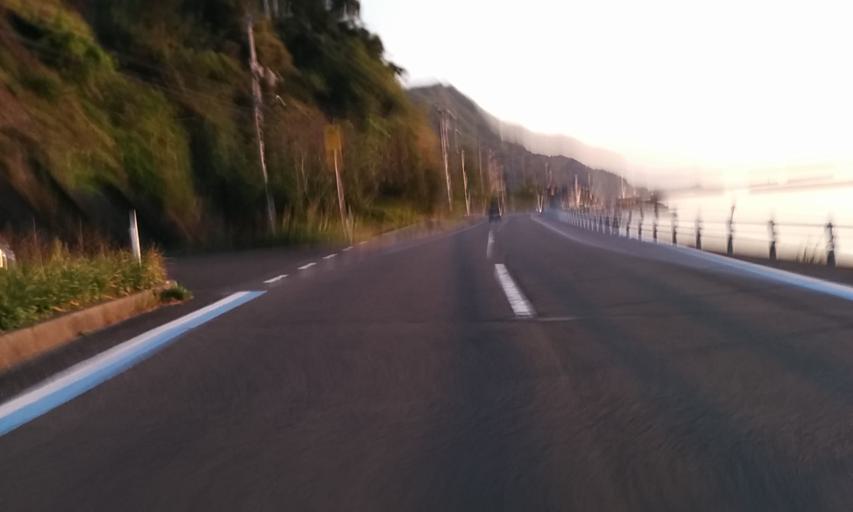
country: JP
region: Ehime
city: Iyo
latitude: 33.6978
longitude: 132.6538
